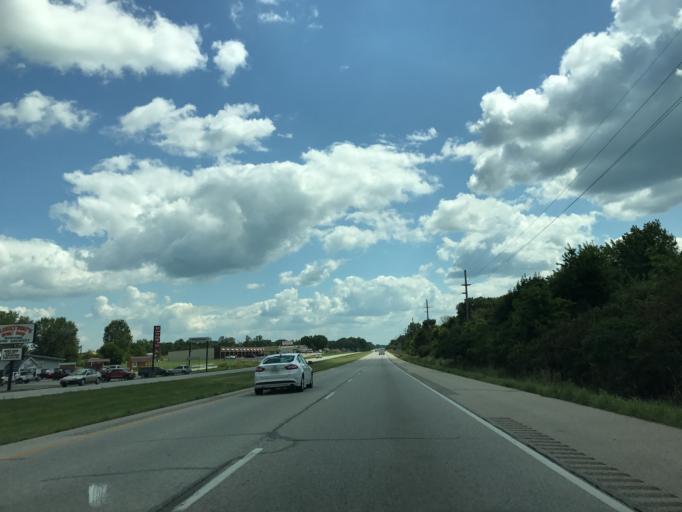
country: US
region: Indiana
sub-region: Kosciusko County
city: Winona Lake
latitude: 41.2205
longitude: -85.7783
